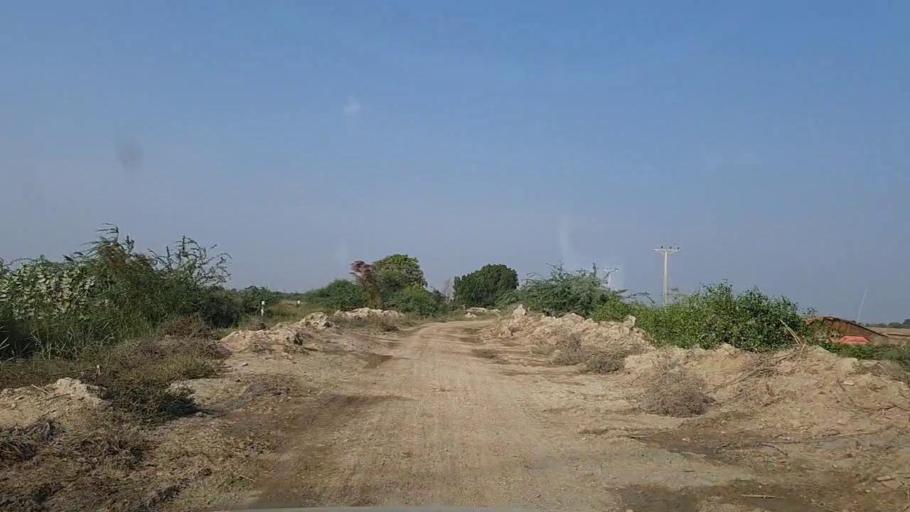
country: PK
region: Sindh
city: Mirpur Sakro
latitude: 24.5846
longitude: 67.5679
